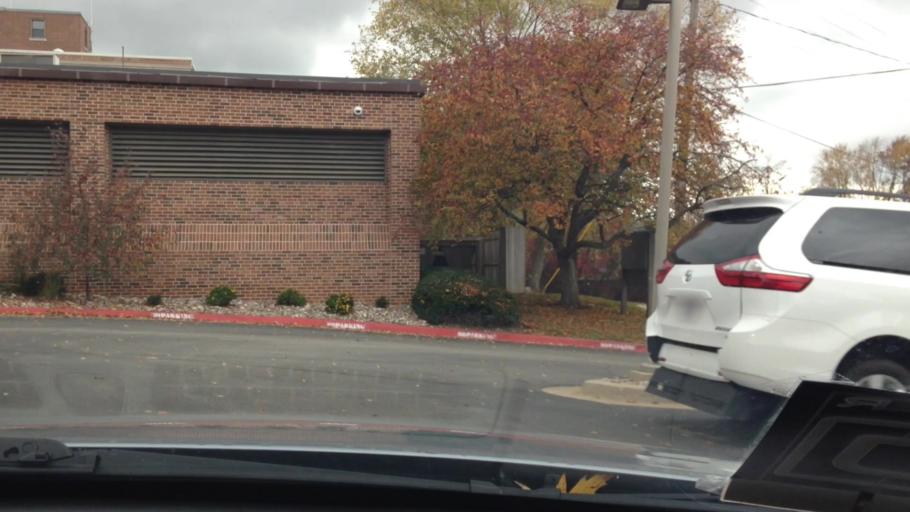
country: US
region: Kansas
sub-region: Leavenworth County
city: Leavenworth
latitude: 39.3075
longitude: -94.9178
